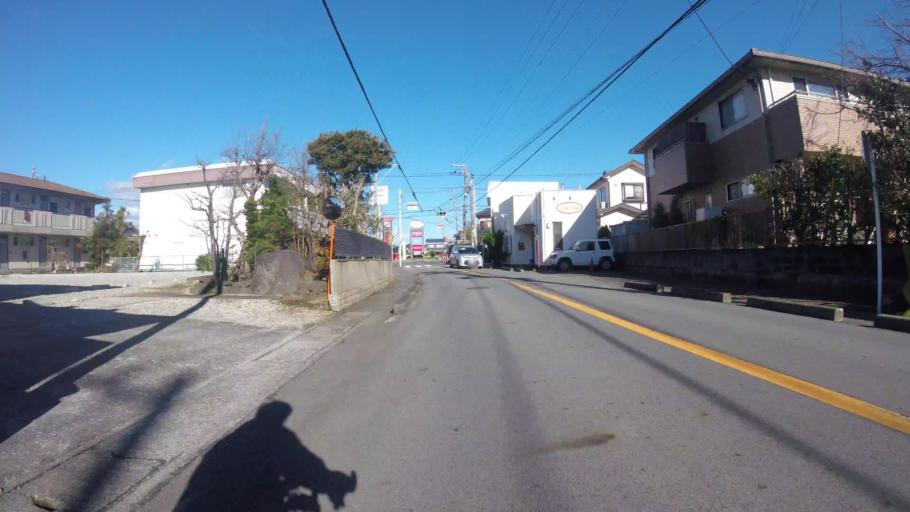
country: JP
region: Shizuoka
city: Numazu
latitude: 35.1051
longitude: 138.8784
